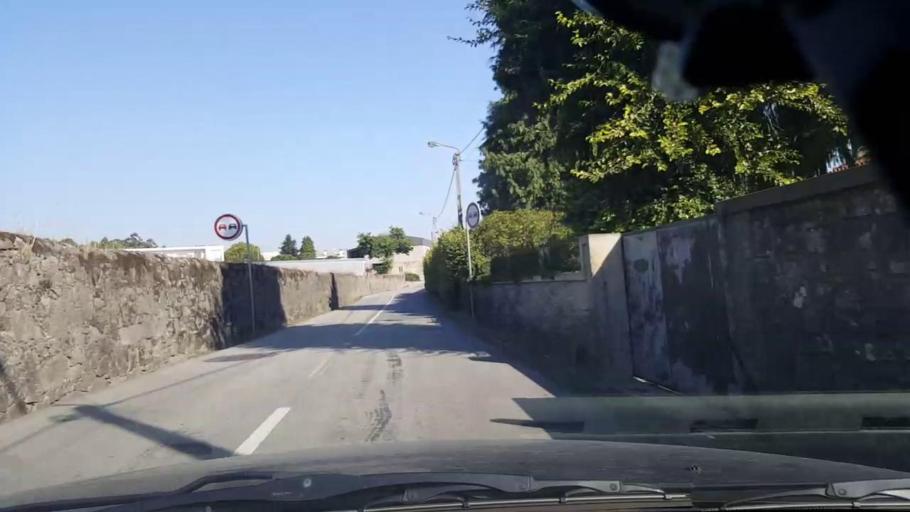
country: PT
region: Porto
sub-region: Vila do Conde
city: Arvore
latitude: 41.3364
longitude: -8.6823
